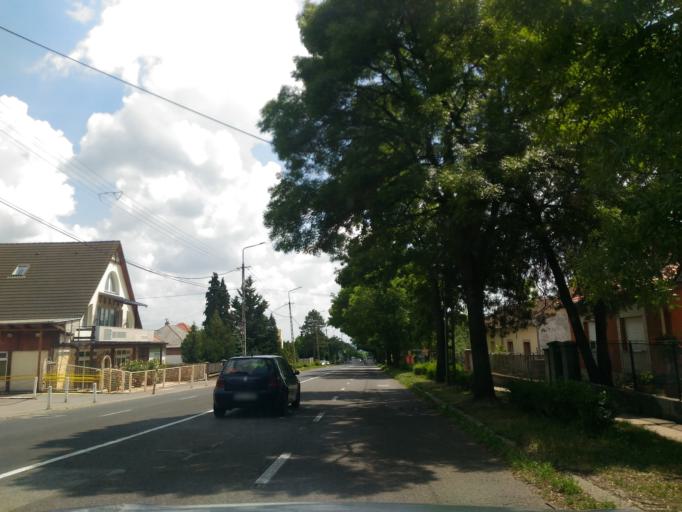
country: HU
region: Baranya
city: Pecs
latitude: 46.1058
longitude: 18.2639
